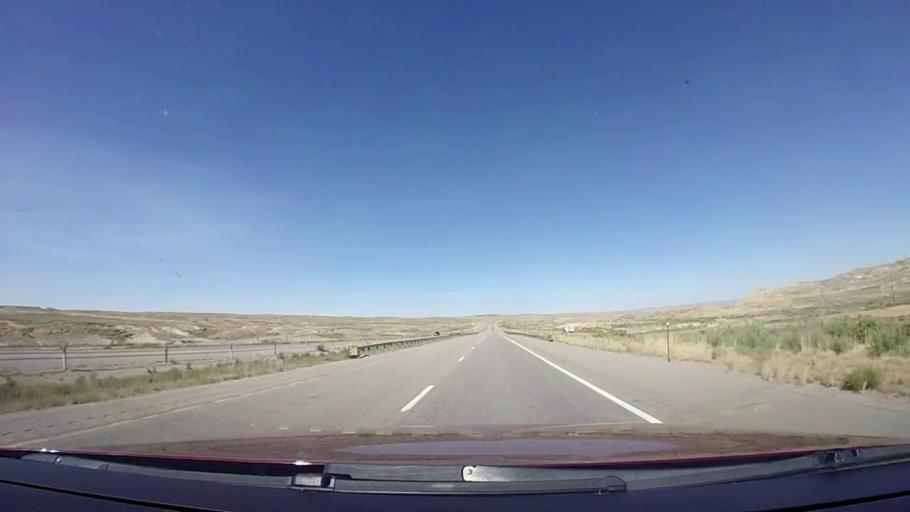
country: US
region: Wyoming
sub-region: Sweetwater County
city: Rock Springs
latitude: 41.6475
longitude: -108.6791
